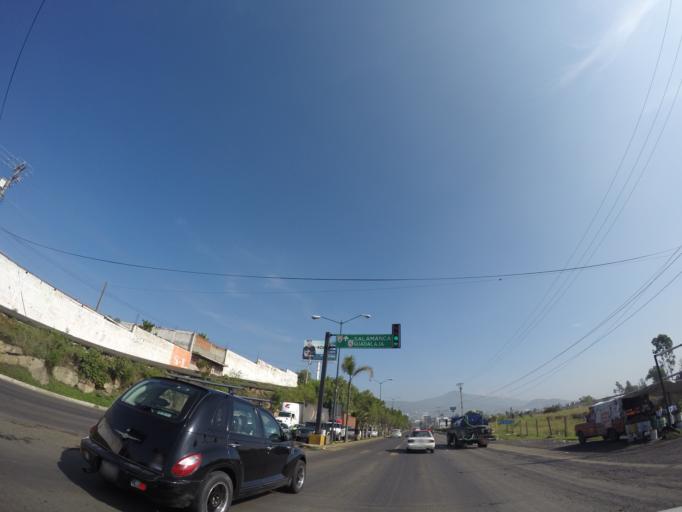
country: MX
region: Michoacan
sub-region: Morelia
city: San Antonio
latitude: 19.6883
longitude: -101.2384
